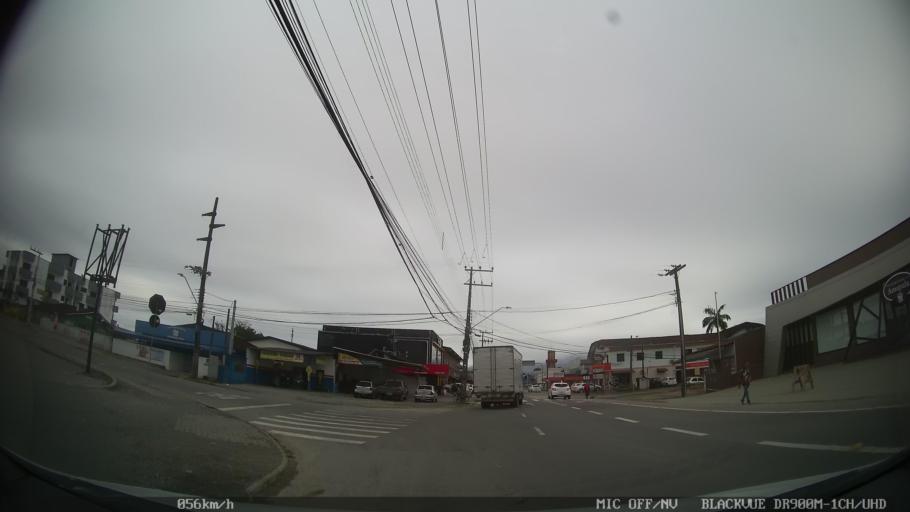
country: BR
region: Santa Catarina
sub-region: Joinville
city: Joinville
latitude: -26.2874
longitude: -48.9004
